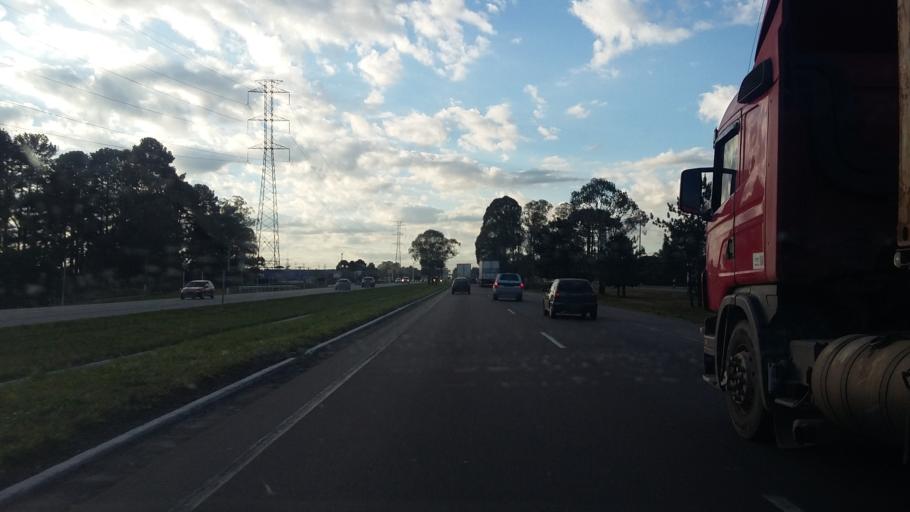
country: BR
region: Parana
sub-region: Curitiba
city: Curitiba
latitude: -25.4454
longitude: -49.3639
